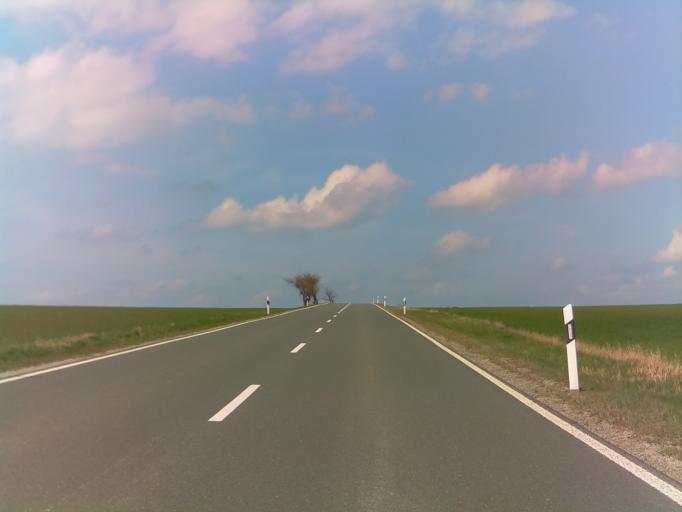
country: DE
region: Thuringia
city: Milda
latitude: 50.8592
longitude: 11.4590
